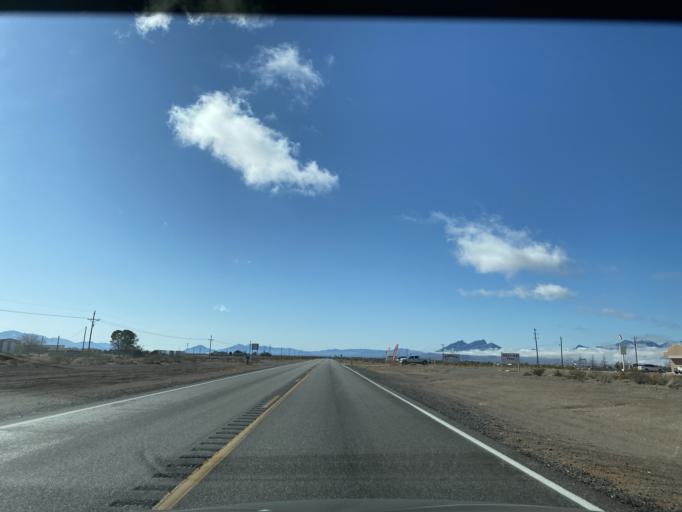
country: US
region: Nevada
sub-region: Nye County
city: Beatty
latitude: 36.5307
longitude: -116.4187
